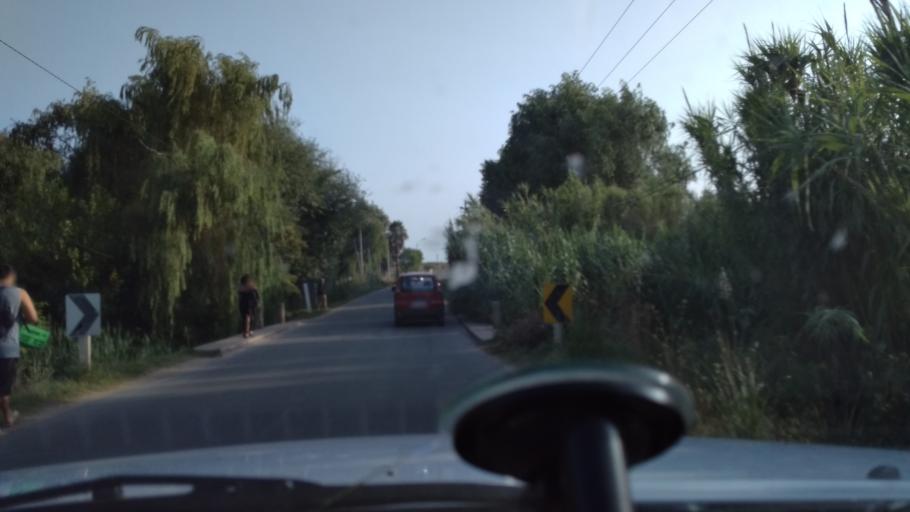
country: UY
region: Canelones
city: Colonia Nicolich
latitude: -34.7778
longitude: -56.0183
